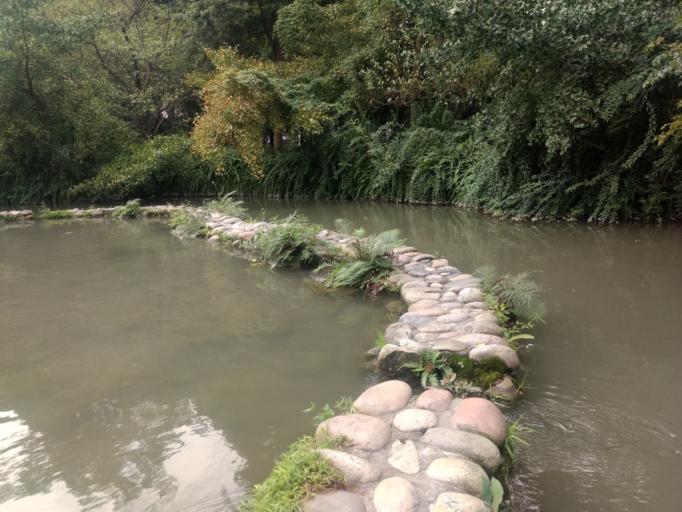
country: CN
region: Sichuan
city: Chengdu
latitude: 30.6639
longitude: 104.0263
